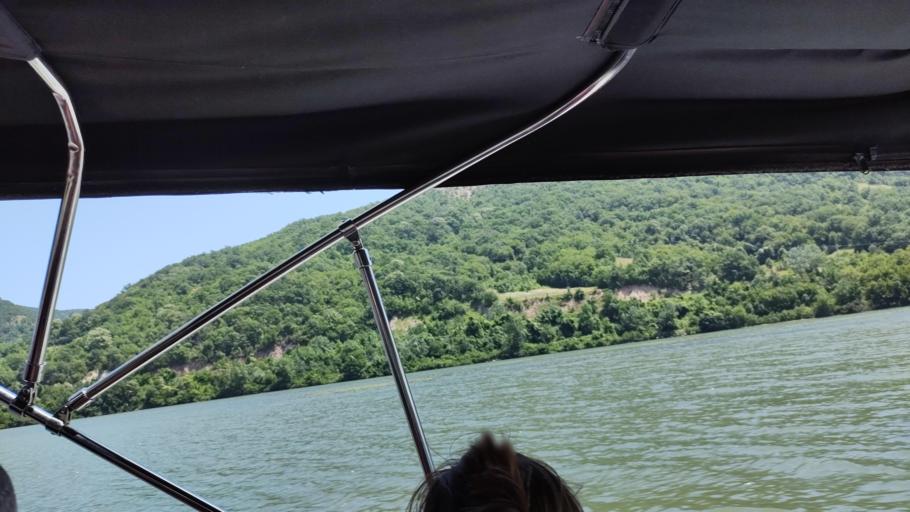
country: RO
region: Caras-Severin
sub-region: Comuna Berzasca
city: Berzasca
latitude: 44.5767
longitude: 22.0288
